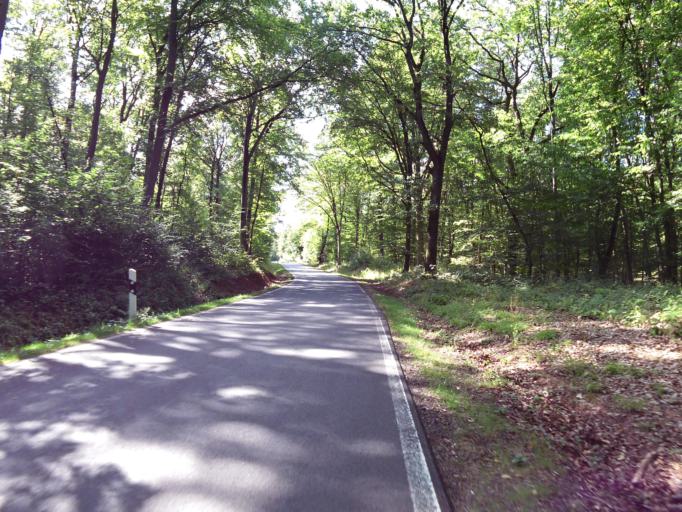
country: DE
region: Rheinland-Pfalz
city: Dreisen
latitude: 49.5836
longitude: 8.0126
